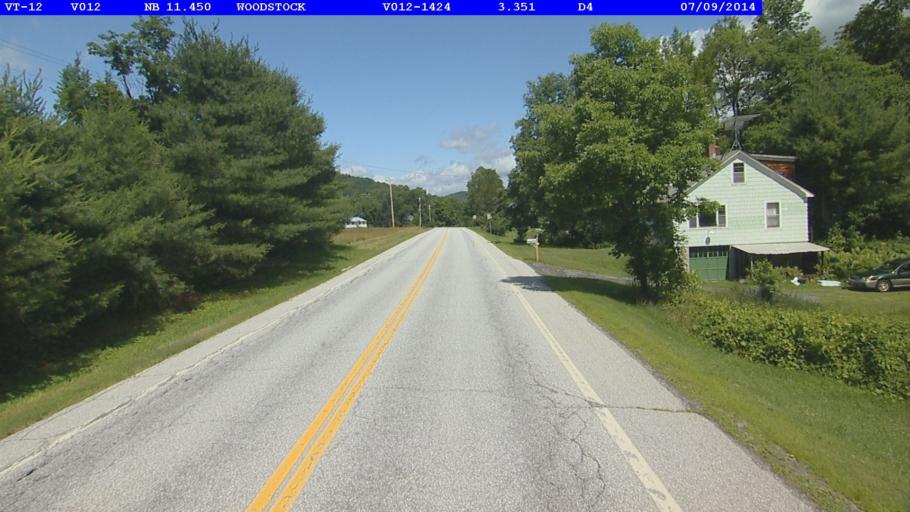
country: US
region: Vermont
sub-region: Windsor County
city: Woodstock
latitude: 43.6496
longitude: -72.5604
